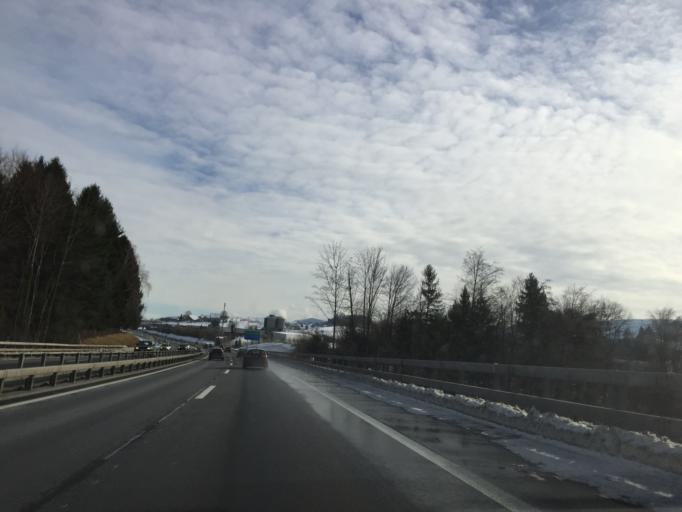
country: CH
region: Zurich
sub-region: Bezirk Horgen
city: Au / Unter-Dorf
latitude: 47.2321
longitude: 8.6228
